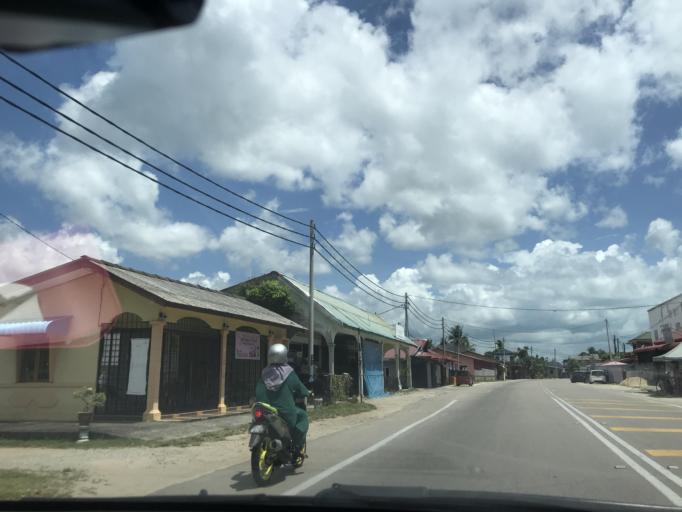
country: TH
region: Narathiwat
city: Tak Bai
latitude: 6.2231
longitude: 102.1067
